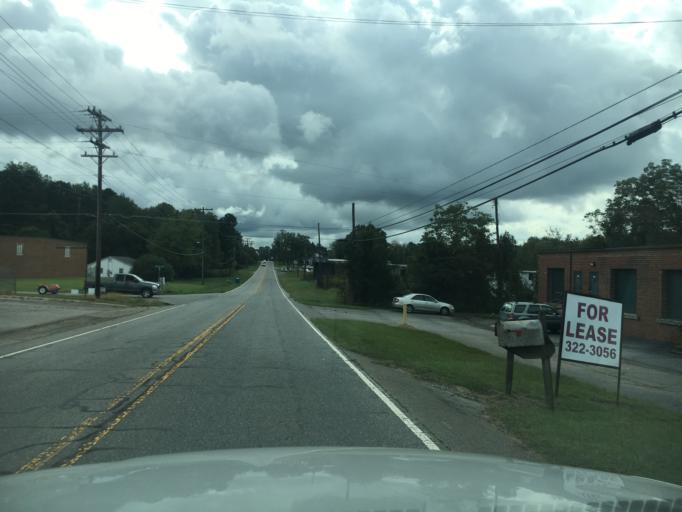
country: US
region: North Carolina
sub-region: Catawba County
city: Saint Stephens
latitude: 35.7259
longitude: -81.2686
